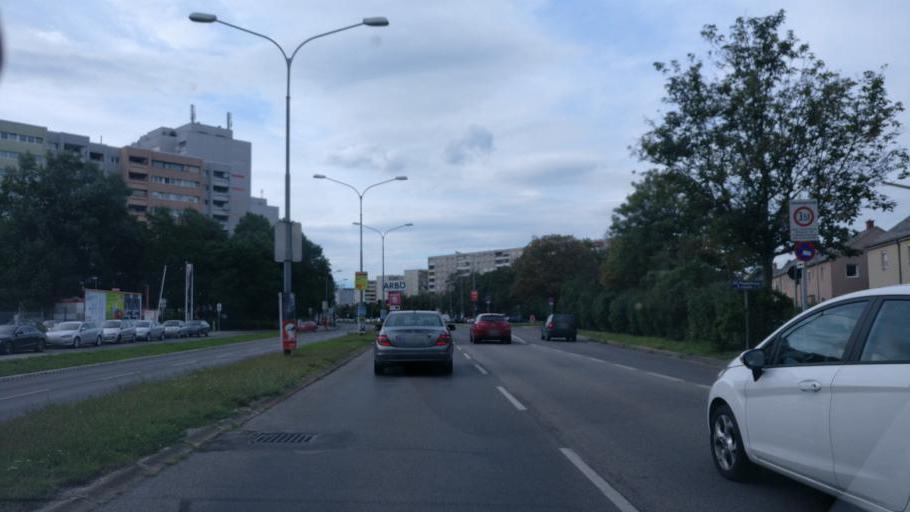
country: AT
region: Lower Austria
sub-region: Politischer Bezirk Wien-Umgebung
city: Gerasdorf bei Wien
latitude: 48.2358
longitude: 16.4425
